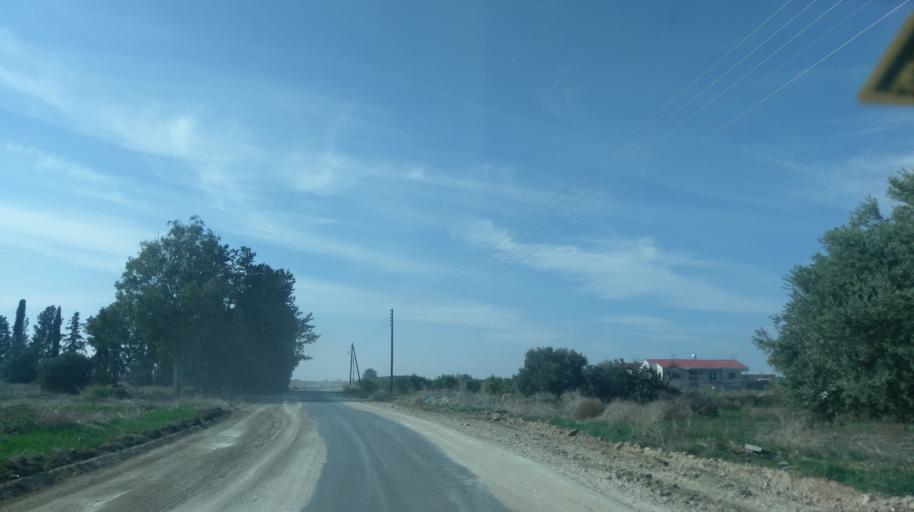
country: CY
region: Larnaka
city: Pergamos
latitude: 35.1530
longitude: 33.6887
